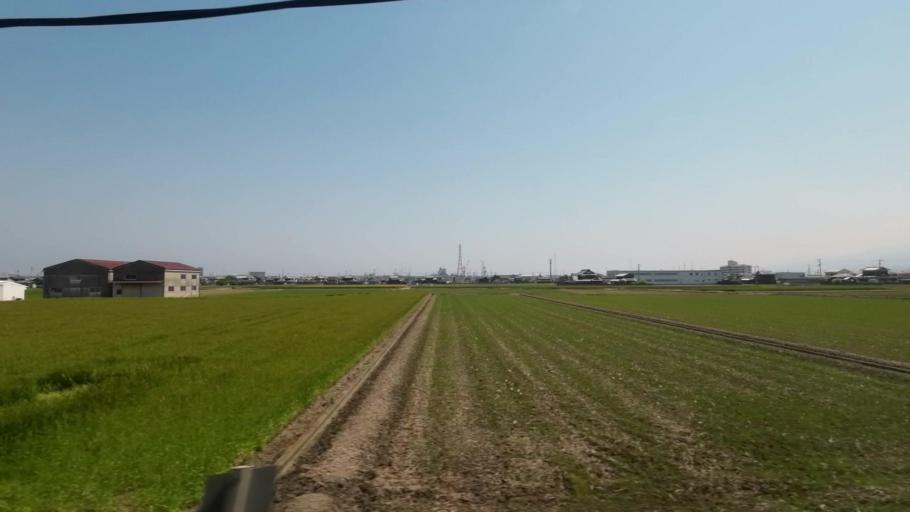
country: JP
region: Ehime
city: Saijo
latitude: 33.9213
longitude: 133.0931
